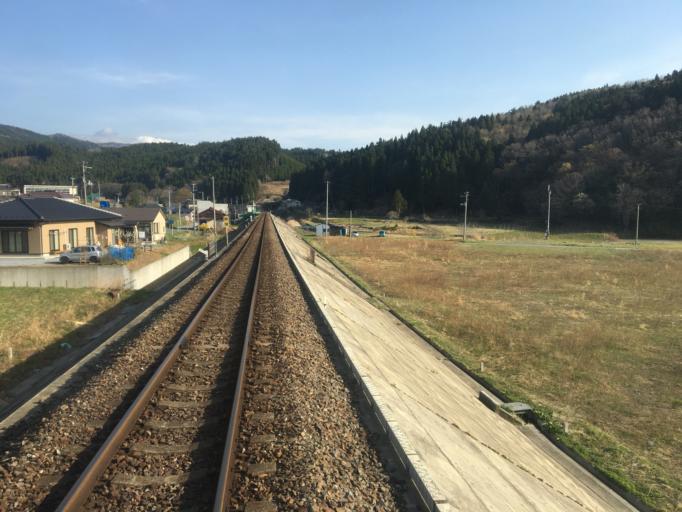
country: JP
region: Iwate
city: Ofunato
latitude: 39.0913
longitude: 141.8071
